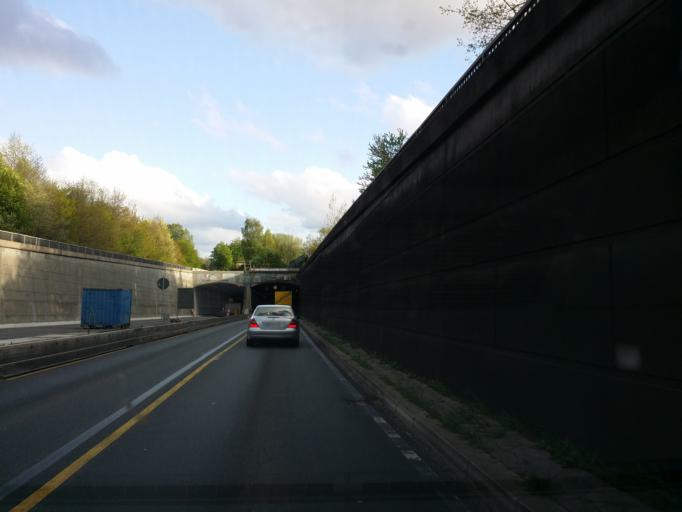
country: DE
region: Schleswig-Holstein
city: Westerronfeld
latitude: 54.2938
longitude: 9.6547
